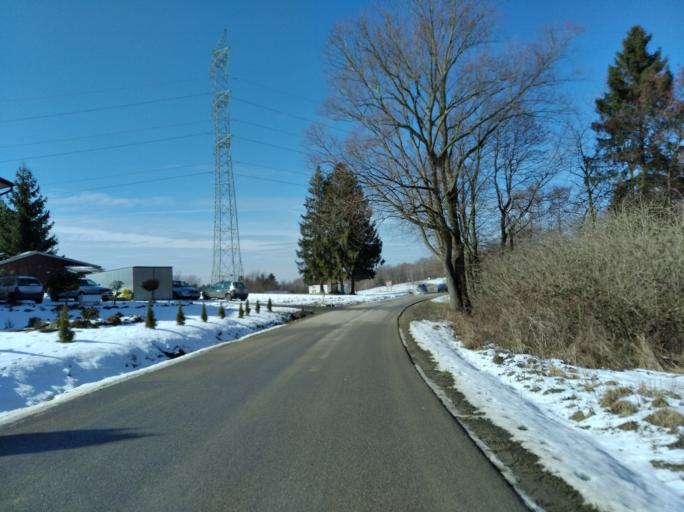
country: PL
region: Subcarpathian Voivodeship
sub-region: Powiat brzozowski
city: Jablonica Polska
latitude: 49.7182
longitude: 21.8936
